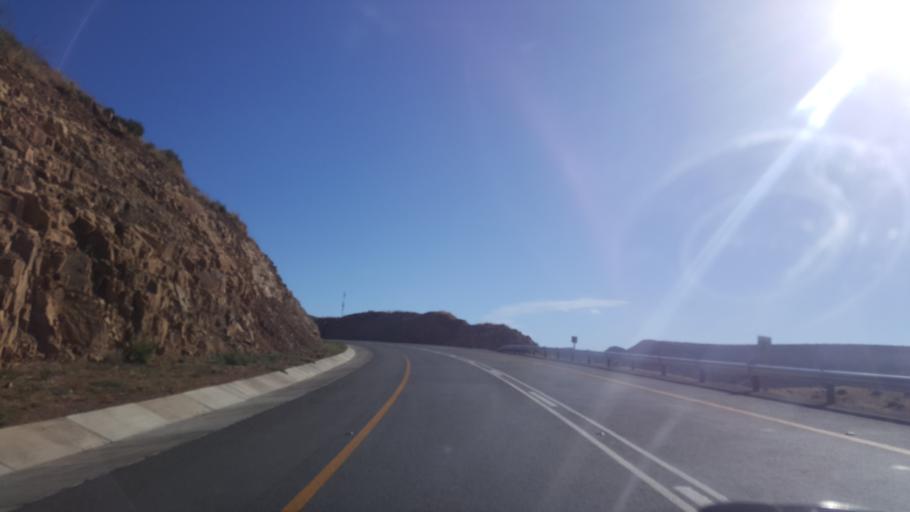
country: ZA
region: Eastern Cape
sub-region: Chris Hani District Municipality
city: Middelburg
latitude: -31.3807
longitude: 25.0338
